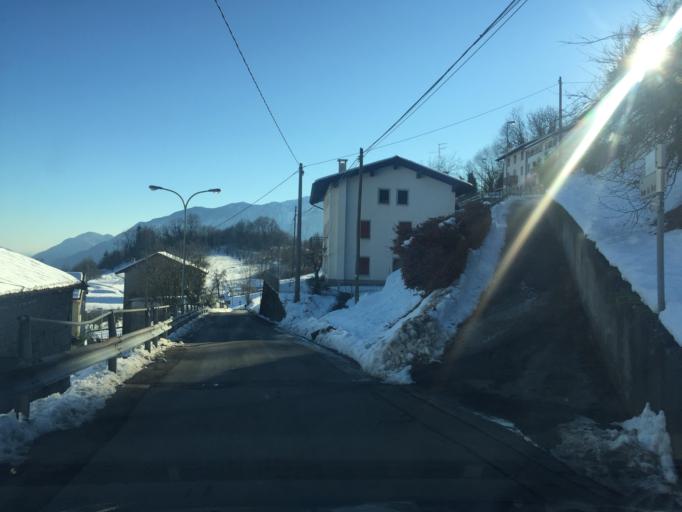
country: IT
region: Friuli Venezia Giulia
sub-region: Provincia di Udine
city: Chiaulis
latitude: 46.4232
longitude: 12.9908
